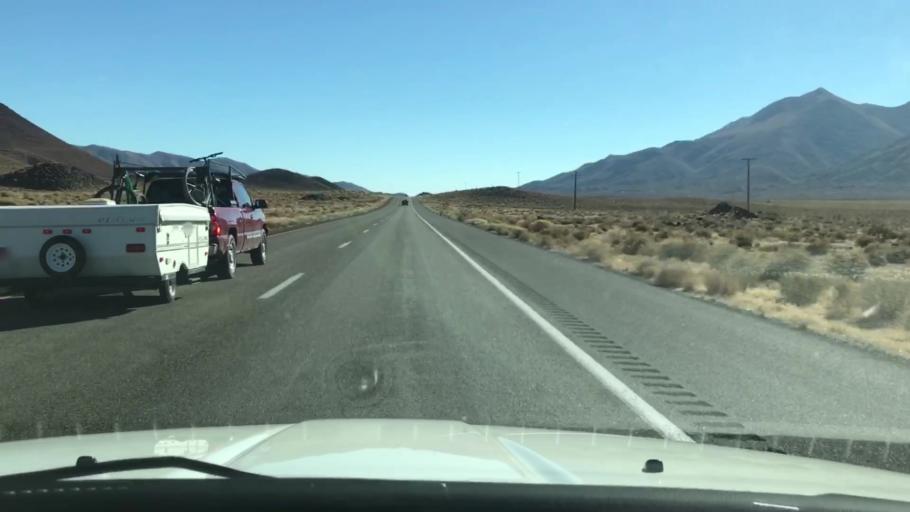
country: US
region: California
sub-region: Kern County
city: Inyokern
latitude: 35.9973
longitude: -117.9325
